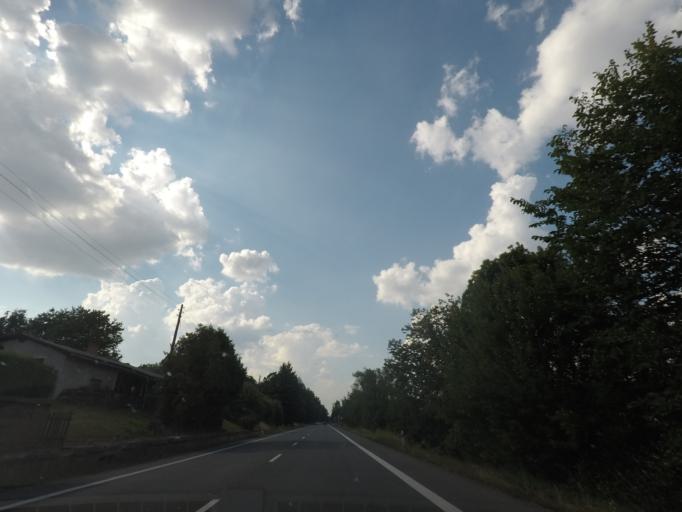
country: CZ
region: Kralovehradecky
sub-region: Okres Nachod
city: Jaromer
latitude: 50.3831
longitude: 15.9140
